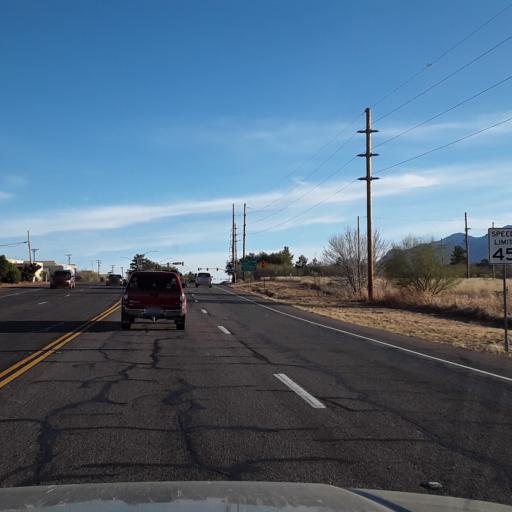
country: US
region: Arizona
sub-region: Cochise County
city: Sierra Vista
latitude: 31.5563
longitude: -110.3079
